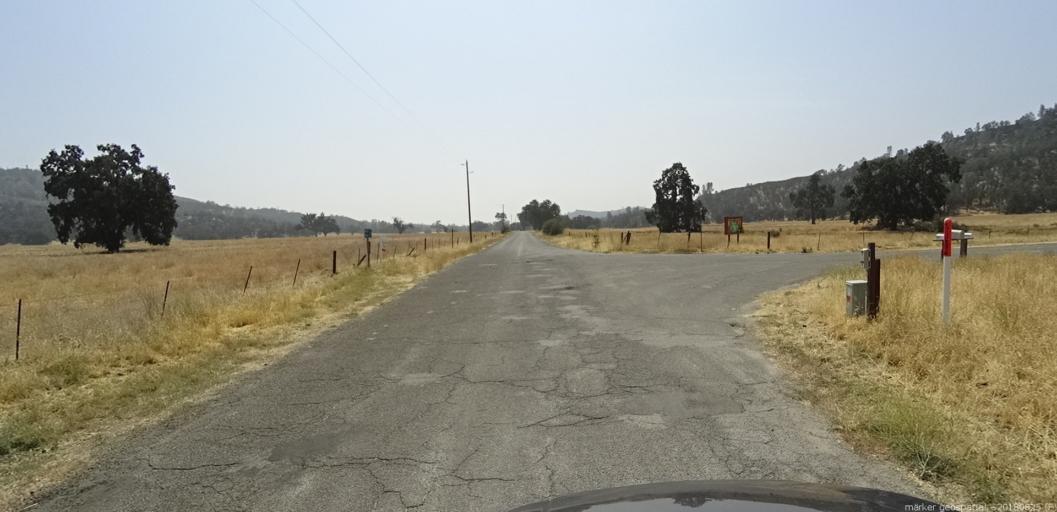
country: US
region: California
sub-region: Fresno County
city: Coalinga
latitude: 35.9271
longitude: -120.5028
